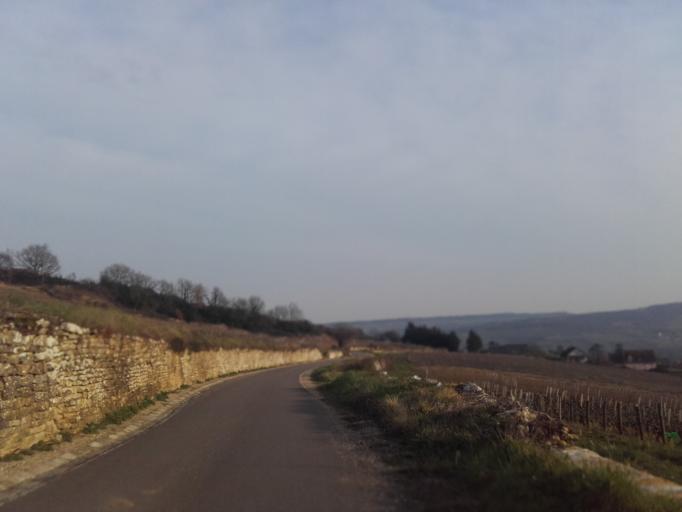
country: FR
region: Bourgogne
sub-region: Departement de la Cote-d'Or
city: Nolay
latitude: 46.9177
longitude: 4.6812
